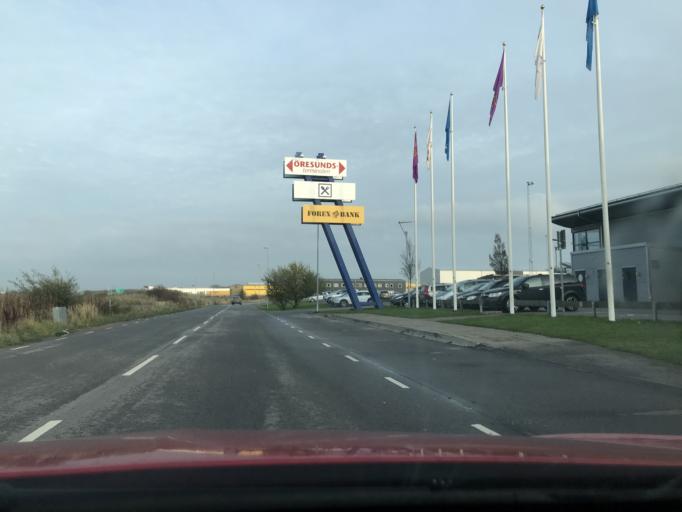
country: SE
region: Skane
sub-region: Burlovs Kommun
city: Arloev
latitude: 55.6084
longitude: 13.0955
